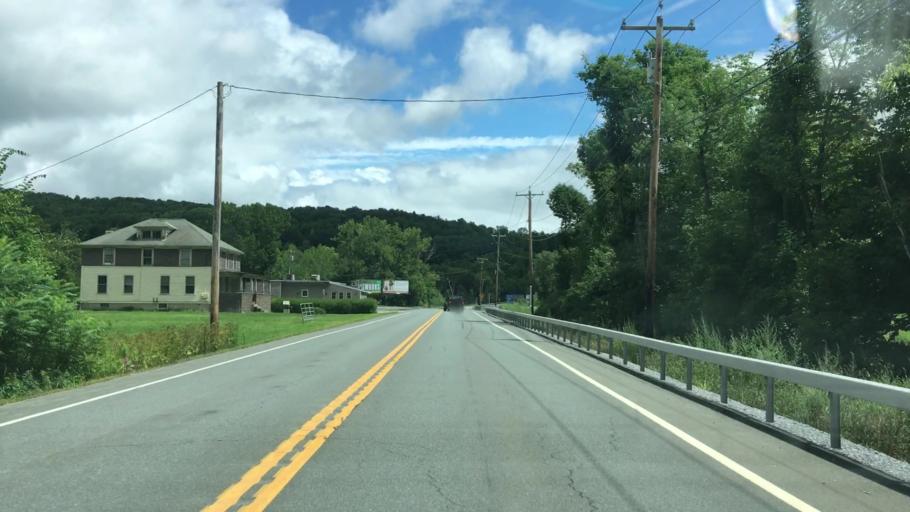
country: US
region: Vermont
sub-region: Bennington County
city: North Bennington
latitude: 42.8787
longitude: -73.2864
